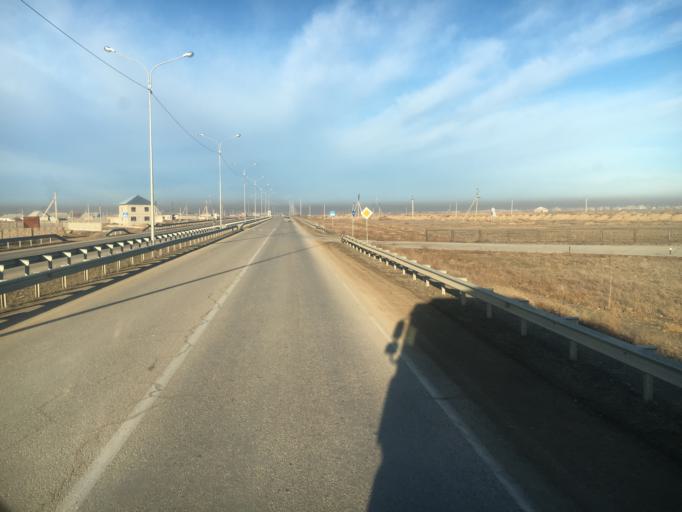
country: KZ
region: Ongtustik Qazaqstan
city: Turkestan
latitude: 43.3025
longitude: 68.3324
